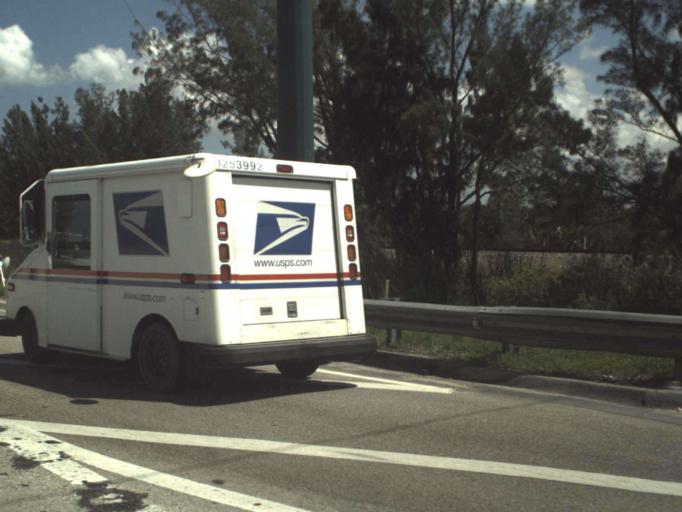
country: US
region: Florida
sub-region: Palm Beach County
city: Palm Beach Gardens
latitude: 26.8101
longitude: -80.1529
